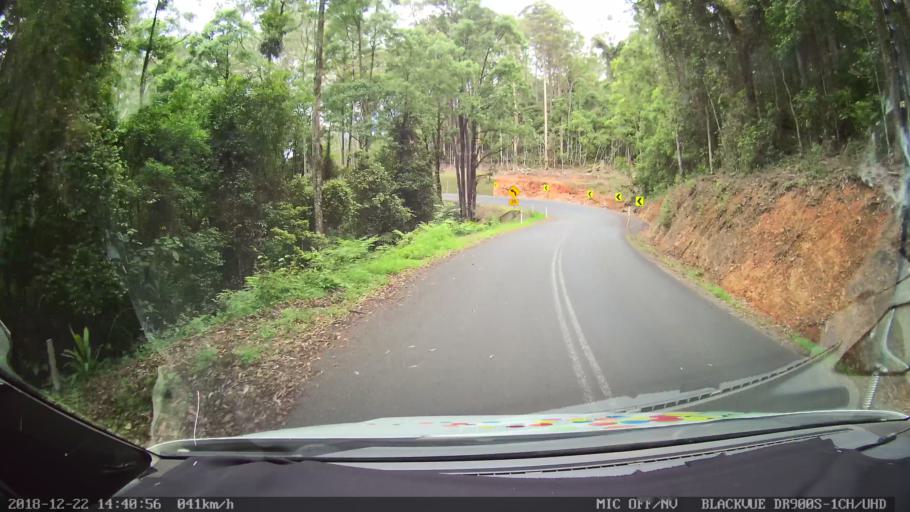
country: AU
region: New South Wales
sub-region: Bellingen
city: Dorrigo
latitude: -30.1518
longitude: 152.5874
